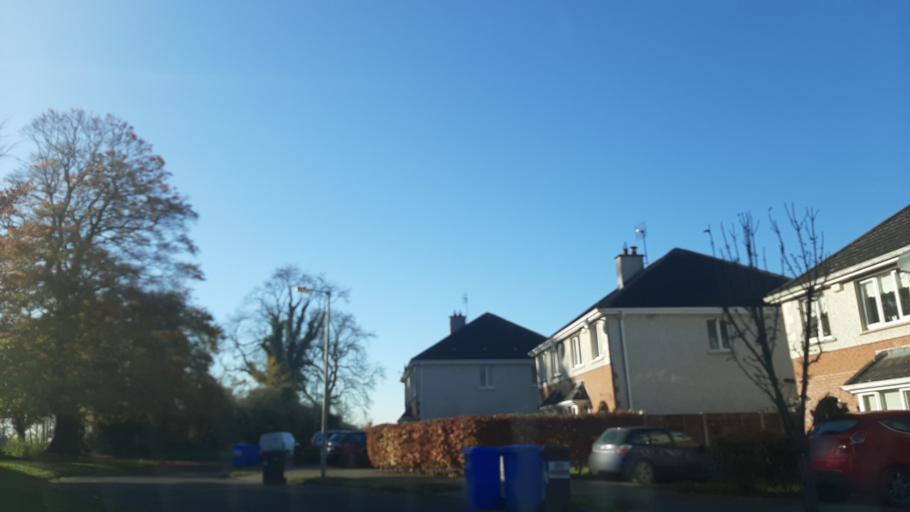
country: IE
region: Leinster
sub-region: Kildare
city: Rathangan
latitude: 53.2186
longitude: -6.9969
